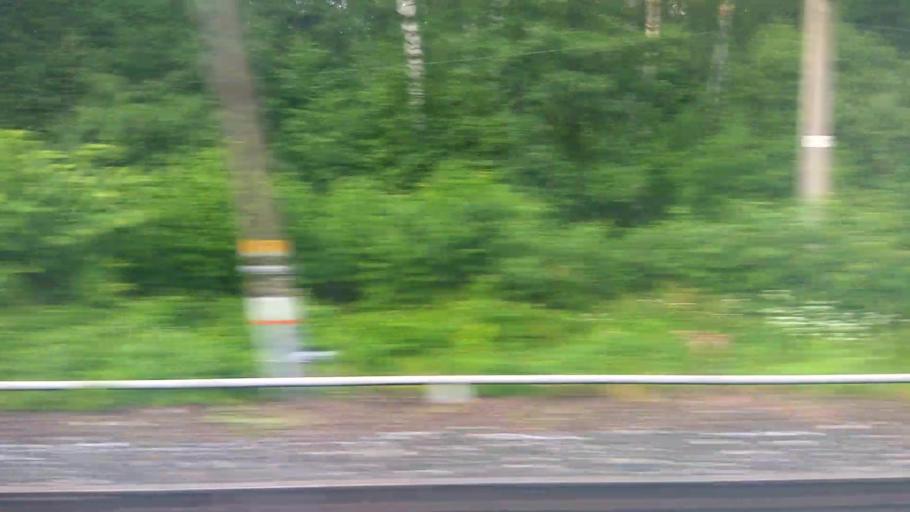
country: RU
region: Moskovskaya
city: Stupino
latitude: 54.9174
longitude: 38.0711
